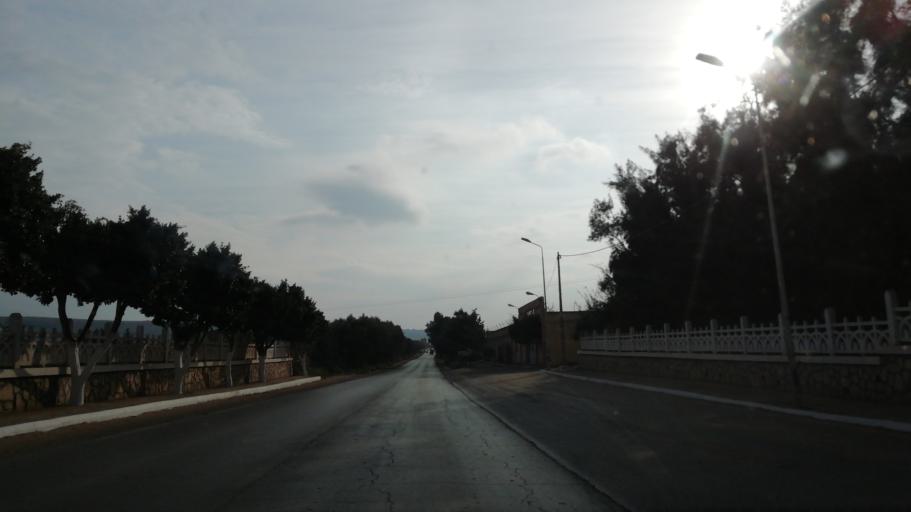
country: DZ
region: Mostaganem
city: Mostaganem
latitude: 35.8530
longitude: 0.0715
